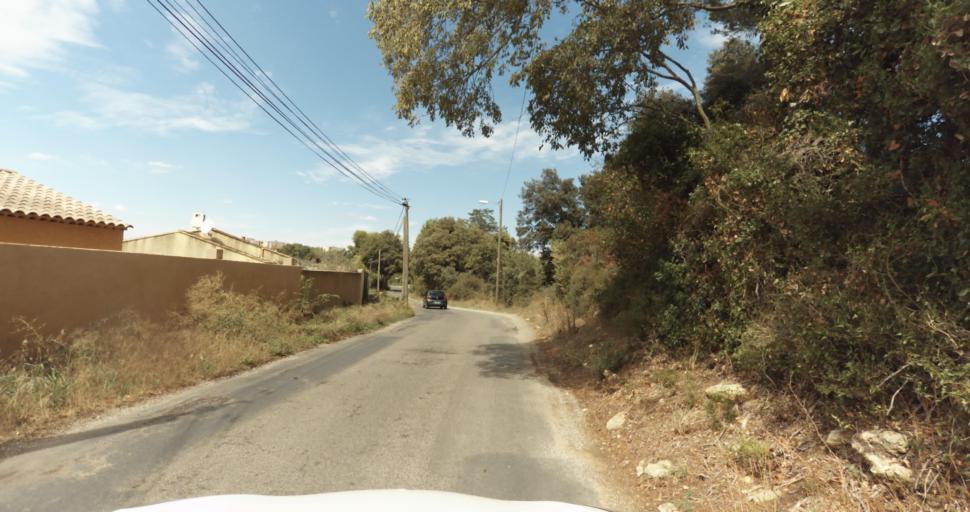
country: FR
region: Provence-Alpes-Cote d'Azur
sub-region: Departement des Bouches-du-Rhone
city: Miramas
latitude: 43.5898
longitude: 5.0168
